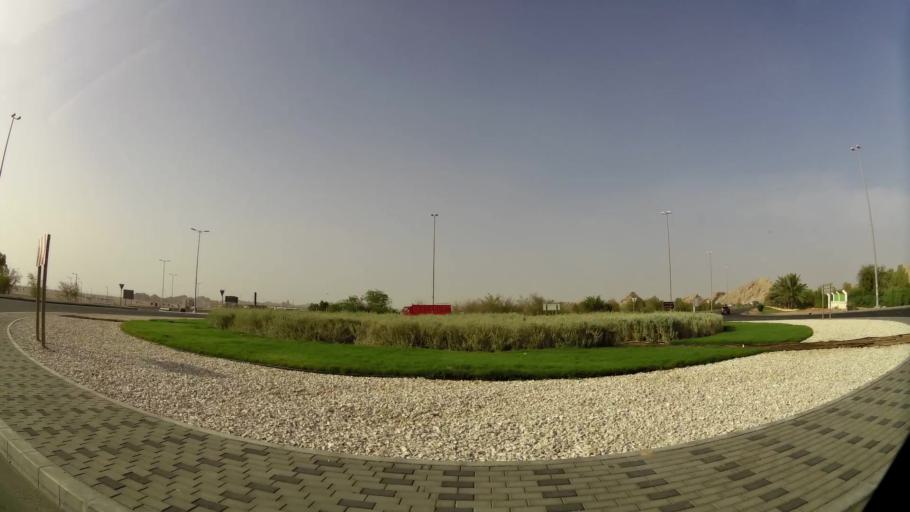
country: AE
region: Abu Dhabi
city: Al Ain
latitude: 24.1085
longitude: 55.7314
